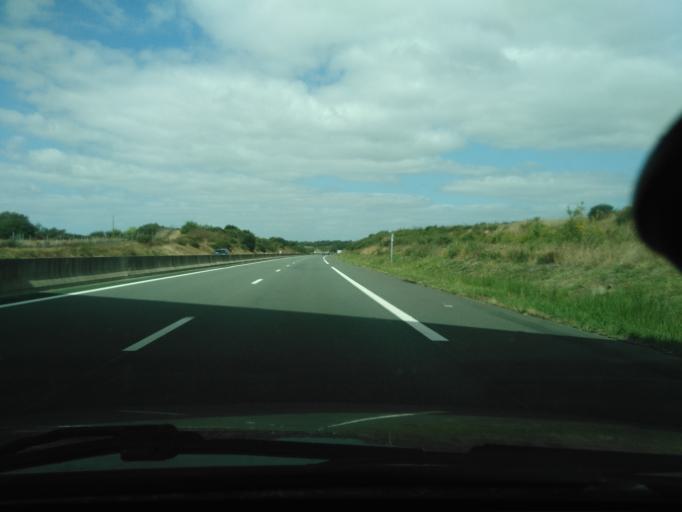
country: FR
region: Pays de la Loire
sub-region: Departement de la Vendee
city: Les Clouzeaux
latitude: 46.6374
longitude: -1.4945
